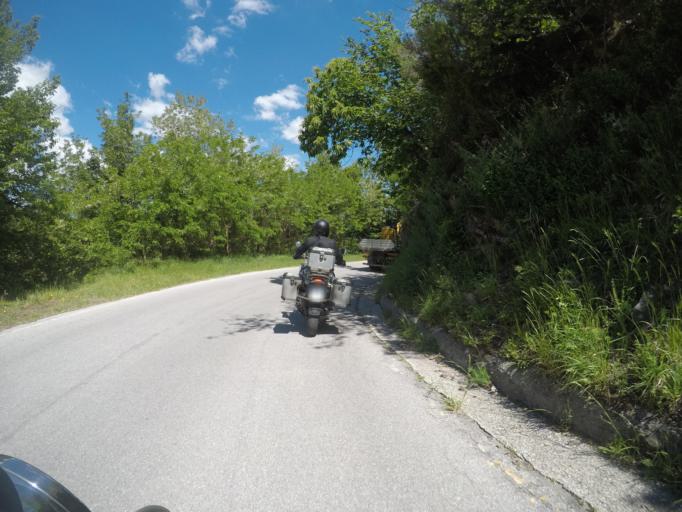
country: IT
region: Tuscany
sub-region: Provincia di Lucca
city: Careggine
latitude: 44.1268
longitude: 10.3348
